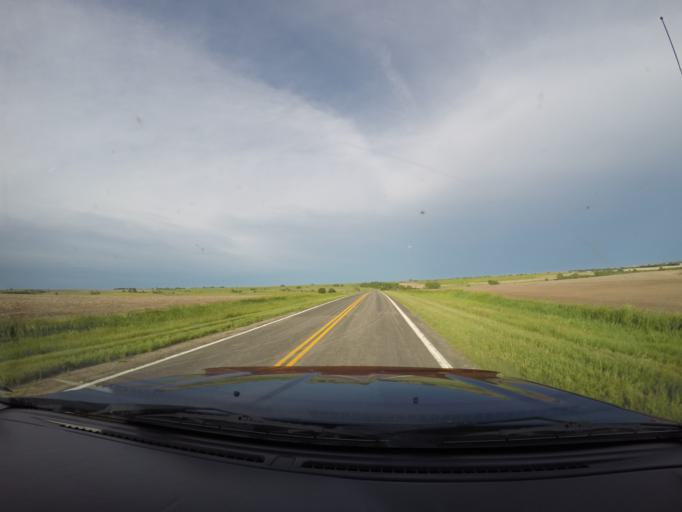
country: US
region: Kansas
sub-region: Smith County
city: Smith Center
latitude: 39.8282
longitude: -98.5687
